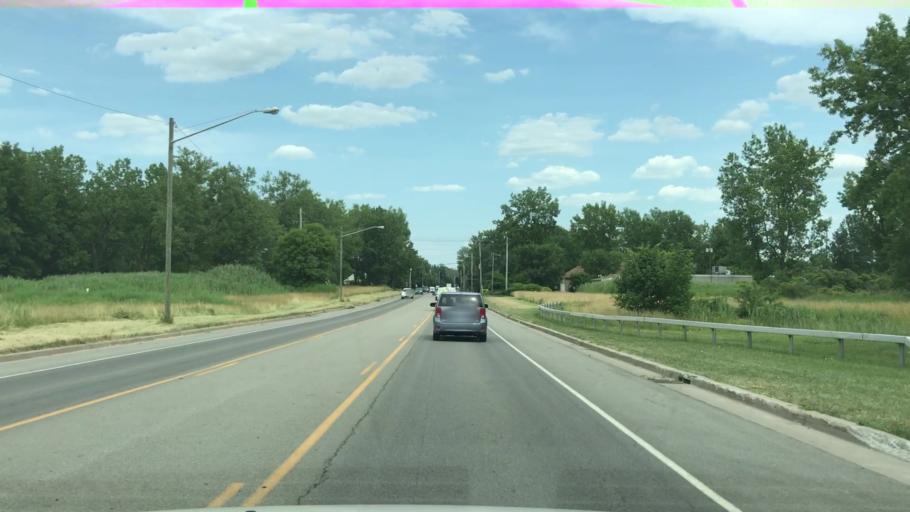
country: US
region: New York
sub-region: Erie County
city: Cheektowaga
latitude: 42.8817
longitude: -78.7388
